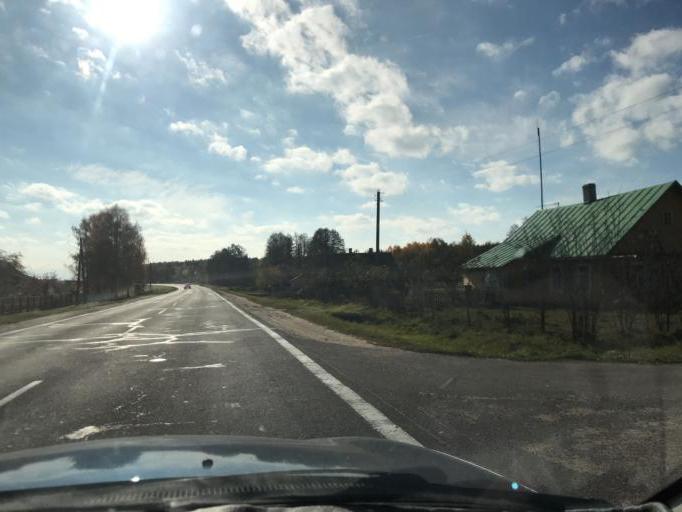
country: LT
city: Salcininkai
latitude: 54.2401
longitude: 25.3548
